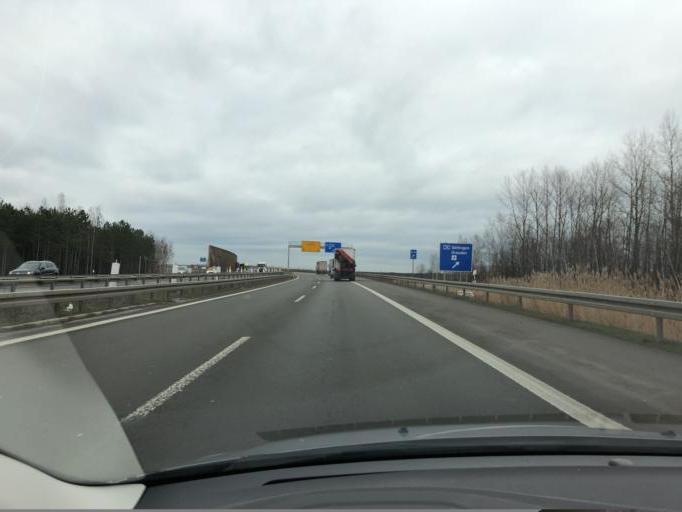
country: DE
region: Saxony
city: Bohlen
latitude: 51.2398
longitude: 12.3914
